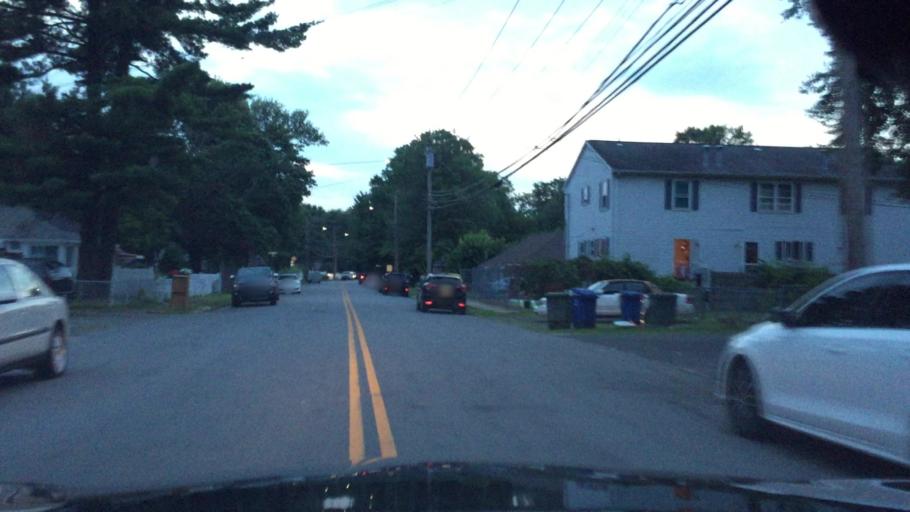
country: US
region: Connecticut
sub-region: Fairfield County
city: Stratford
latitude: 41.2008
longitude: -73.1612
